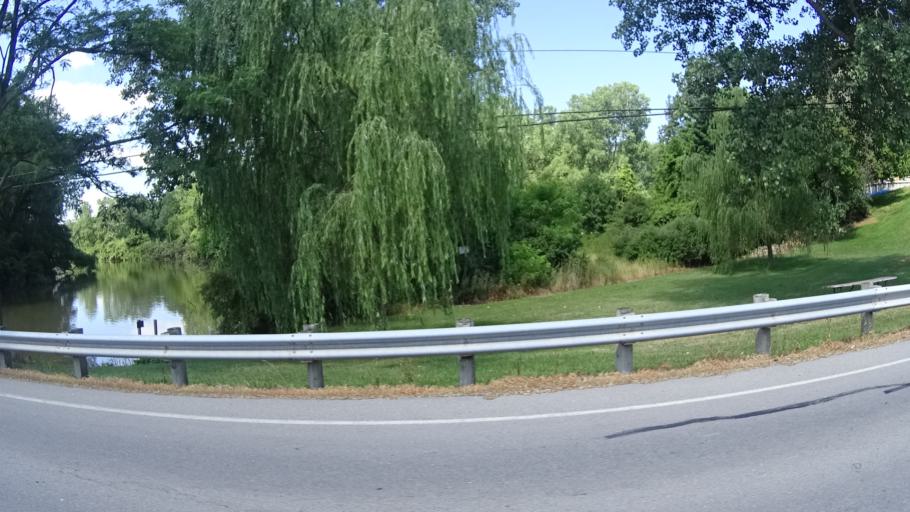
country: US
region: Ohio
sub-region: Erie County
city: Huron
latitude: 41.3788
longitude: -82.5662
